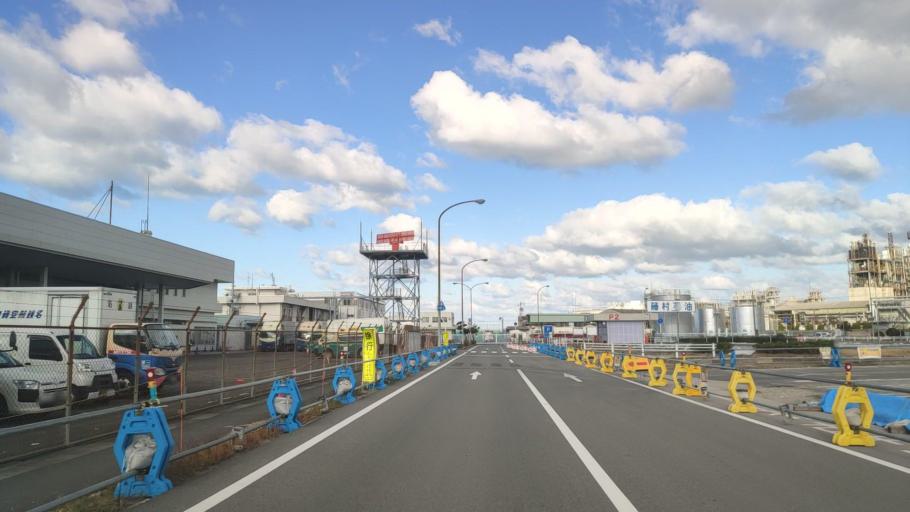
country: JP
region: Ehime
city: Masaki-cho
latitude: 33.8301
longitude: 132.7011
